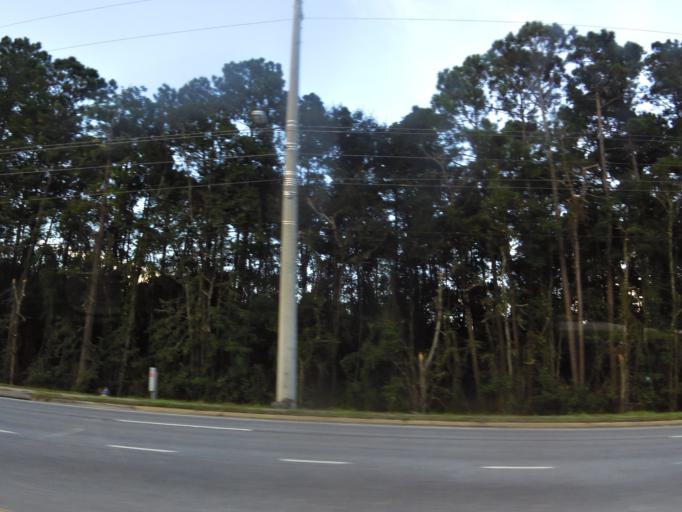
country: US
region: Georgia
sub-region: Camden County
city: St Marys
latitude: 30.7588
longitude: -81.5994
